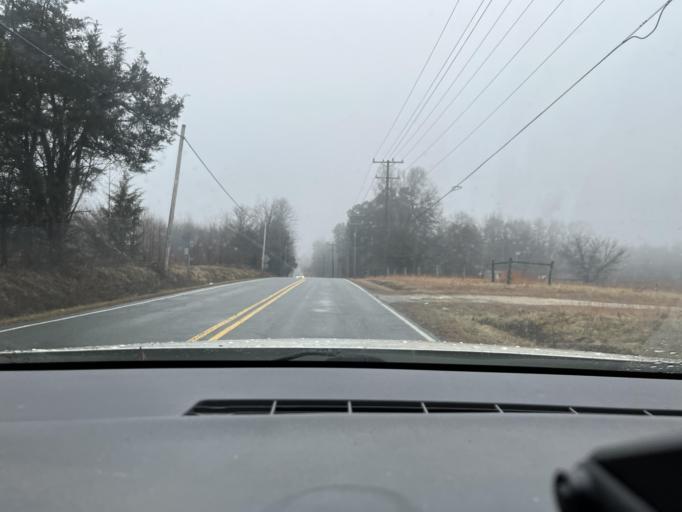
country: US
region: North Carolina
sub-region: Guilford County
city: Pleasant Garden
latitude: 35.9819
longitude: -79.7774
